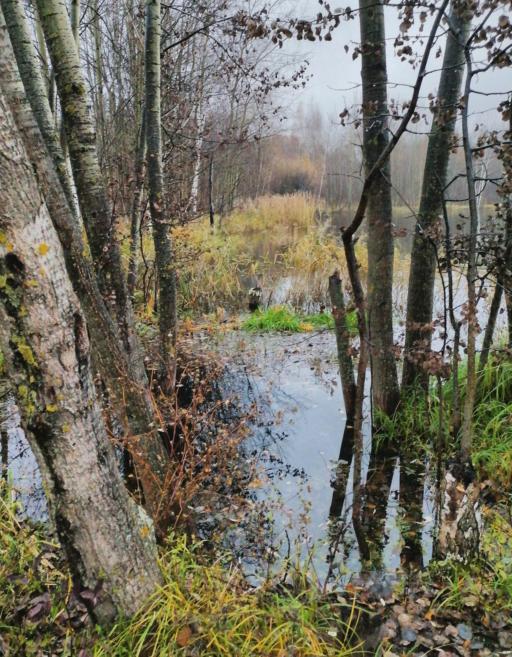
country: RU
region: Moskovskaya
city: Khoroshevo-Mnevniki
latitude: 55.7649
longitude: 37.4510
